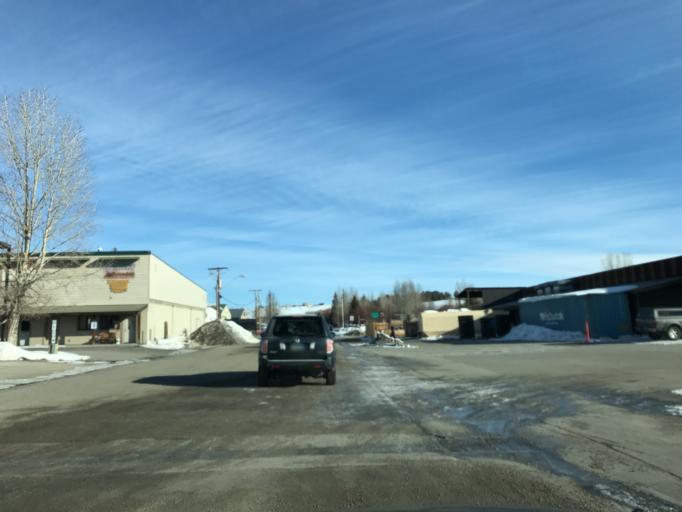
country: US
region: Wyoming
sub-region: Sublette County
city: Pinedale
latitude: 42.8668
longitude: -109.8572
